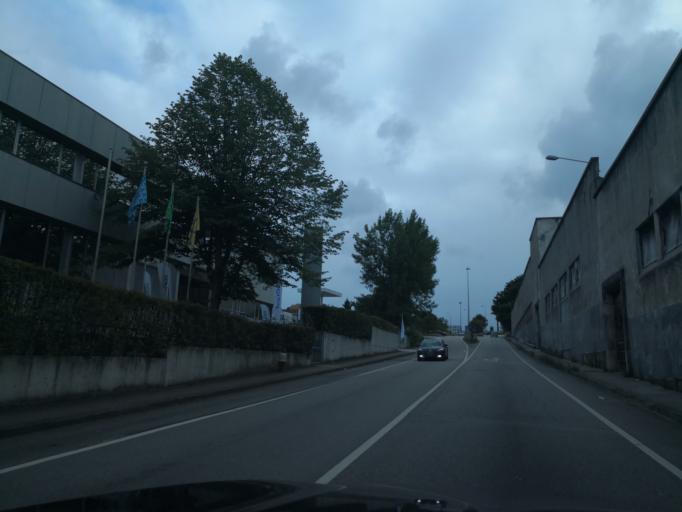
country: PT
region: Porto
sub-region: Gondomar
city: Rio Tinto
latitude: 41.1699
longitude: -8.5710
